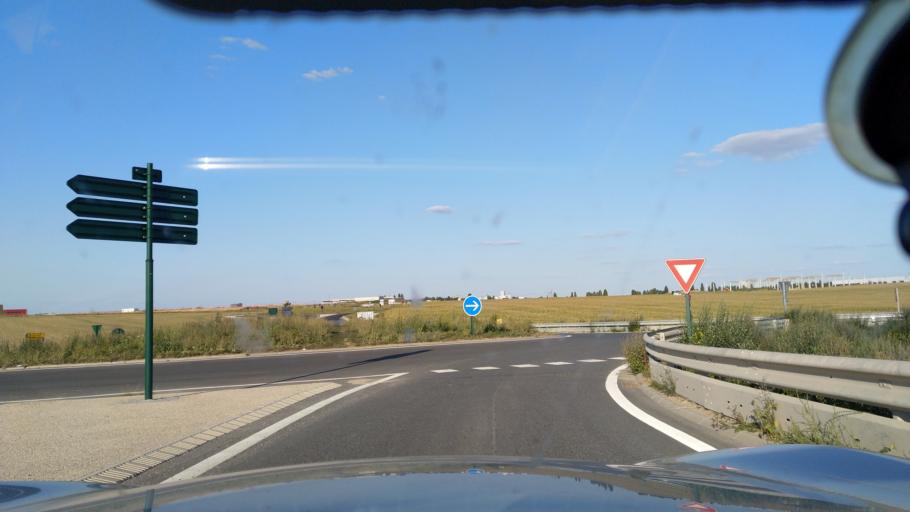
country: FR
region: Ile-de-France
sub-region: Departement du Val-d'Oise
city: Puiseux-en-France
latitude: 49.0438
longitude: 2.4800
